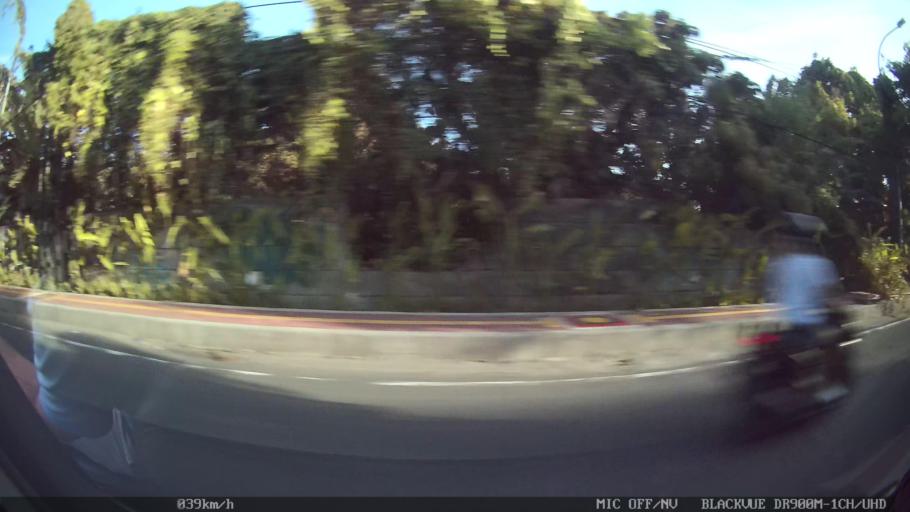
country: ID
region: Bali
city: Jimbaran
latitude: -8.7813
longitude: 115.1762
